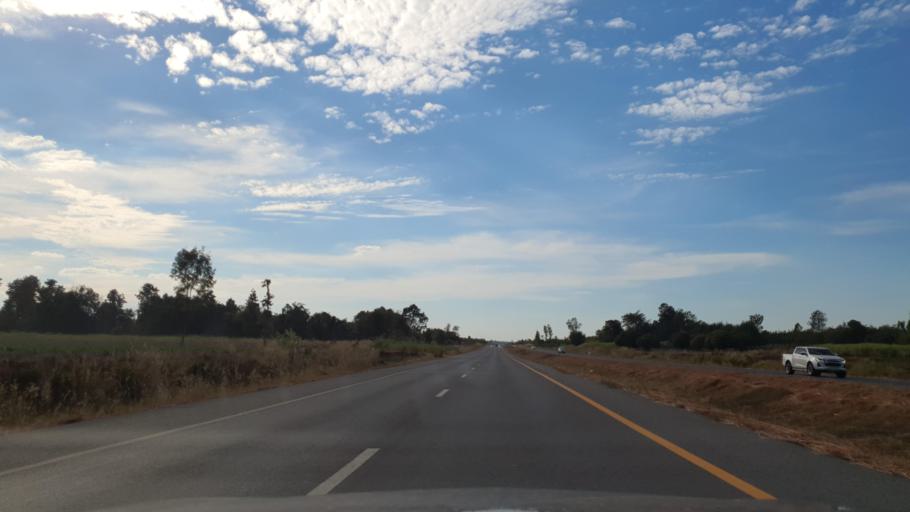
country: TH
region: Roi Et
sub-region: Amphoe Pho Chai
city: Pho Chai
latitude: 16.4130
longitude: 103.7772
